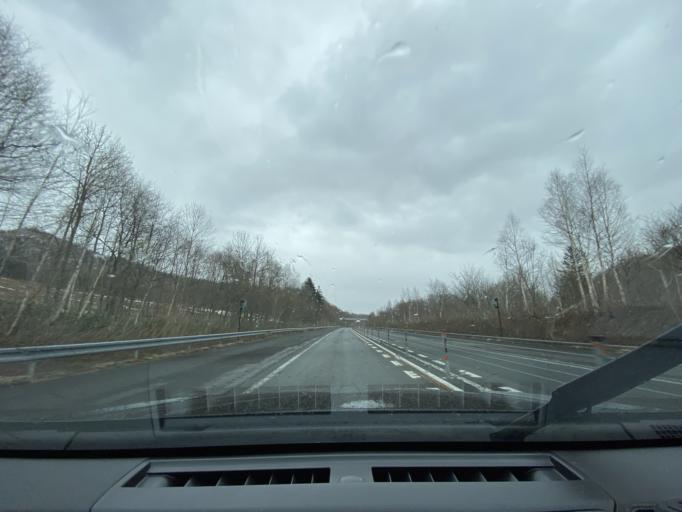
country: JP
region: Hokkaido
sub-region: Asahikawa-shi
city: Asahikawa
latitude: 43.9496
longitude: 142.4695
